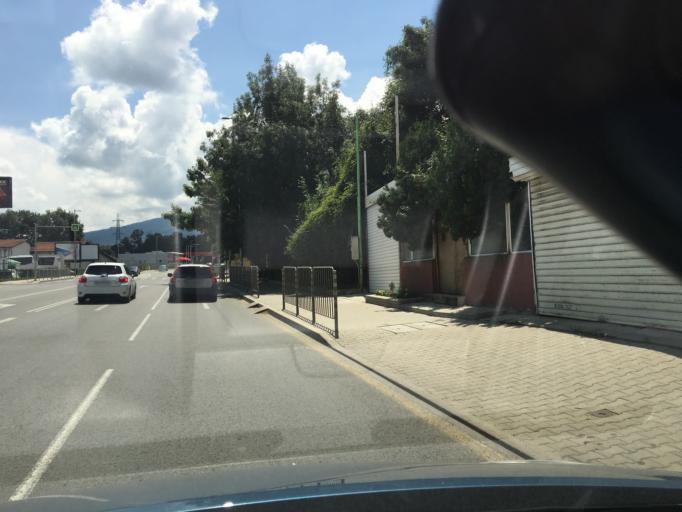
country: BG
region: Sofia-Capital
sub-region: Stolichna Obshtina
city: Sofia
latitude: 42.6535
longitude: 23.3158
